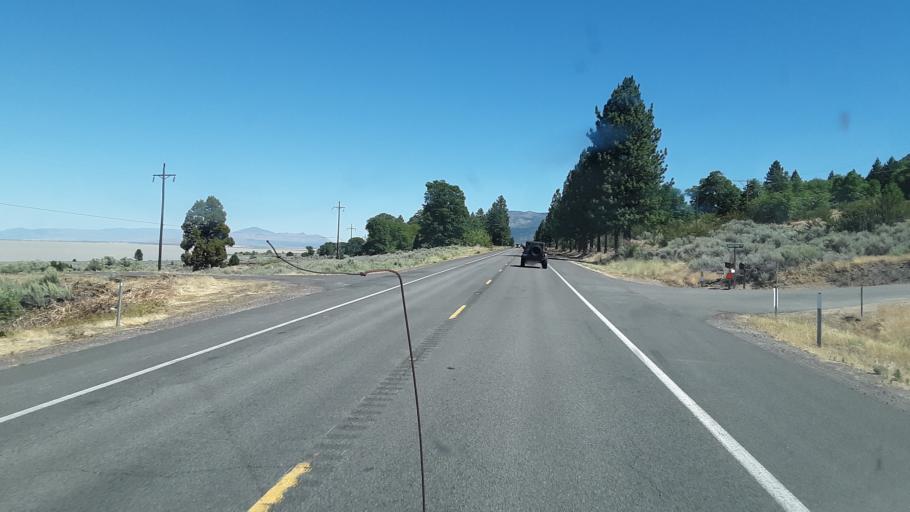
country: US
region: California
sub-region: Lassen County
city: Janesville
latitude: 40.2243
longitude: -120.4360
